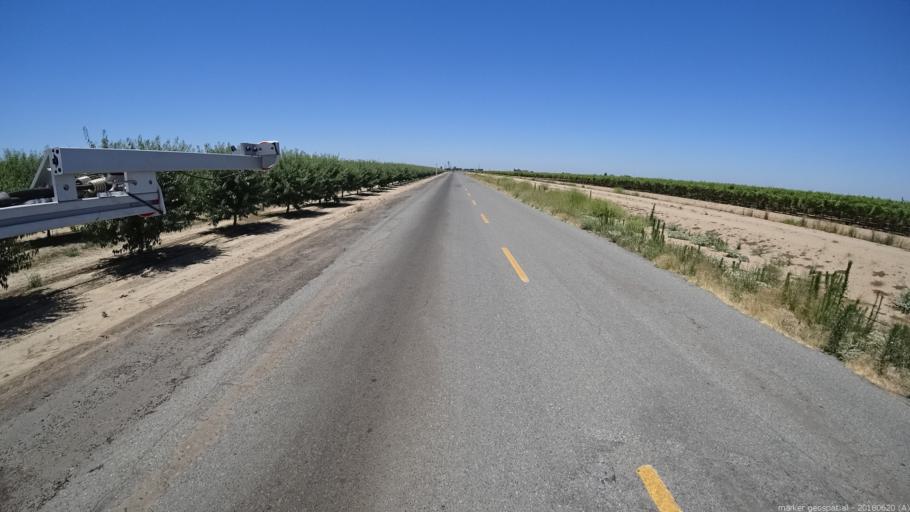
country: US
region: California
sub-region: Fresno County
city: Biola
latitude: 36.8657
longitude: -119.9881
